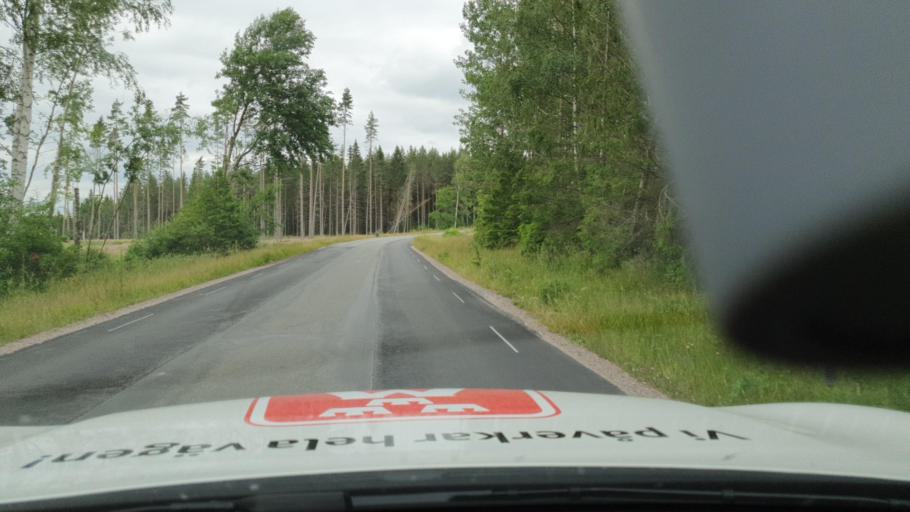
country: SE
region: Vaestra Goetaland
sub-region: Tidaholms Kommun
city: Olofstorp
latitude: 58.3512
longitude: 13.9599
